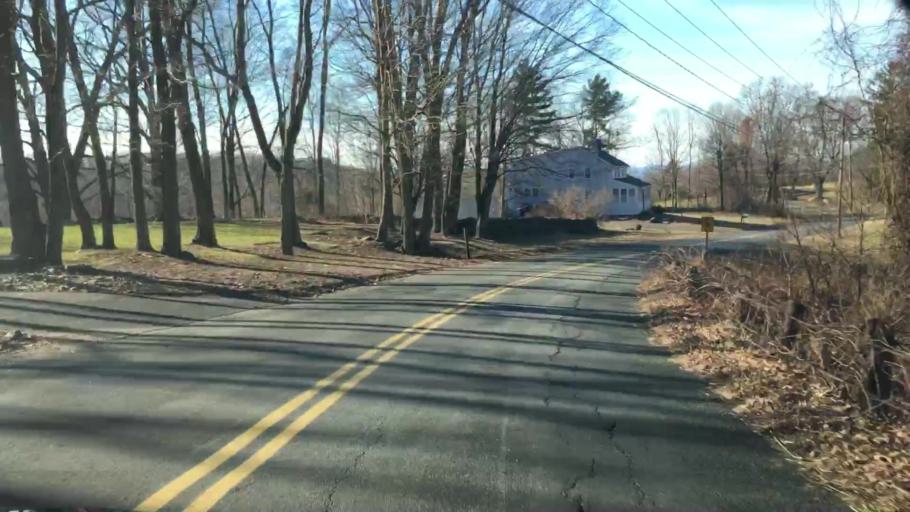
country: US
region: Connecticut
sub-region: Tolland County
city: Somers
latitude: 41.9691
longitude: -72.4256
